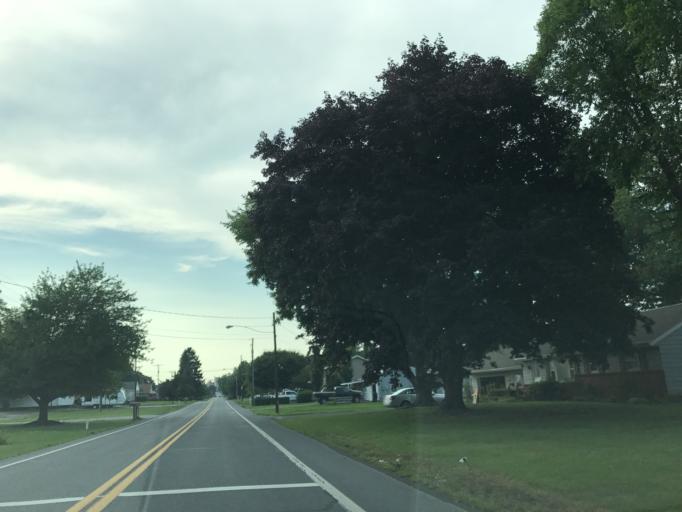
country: US
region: Pennsylvania
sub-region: Lancaster County
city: Rheems
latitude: 40.1258
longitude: -76.5570
